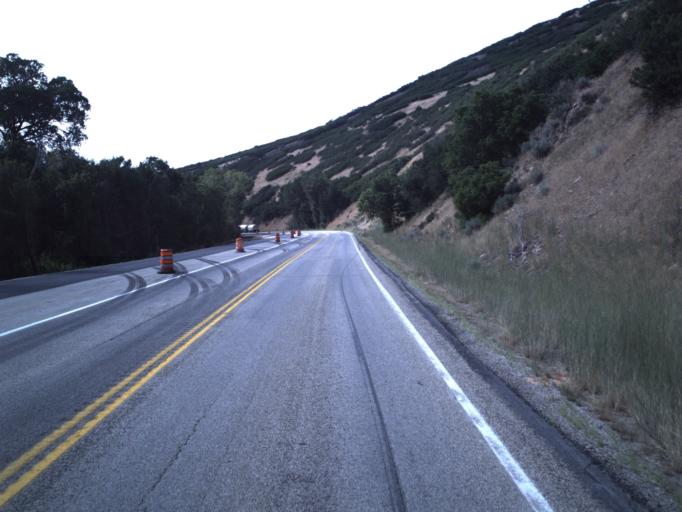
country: US
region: Utah
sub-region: Wasatch County
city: Heber
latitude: 40.4173
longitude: -111.3336
